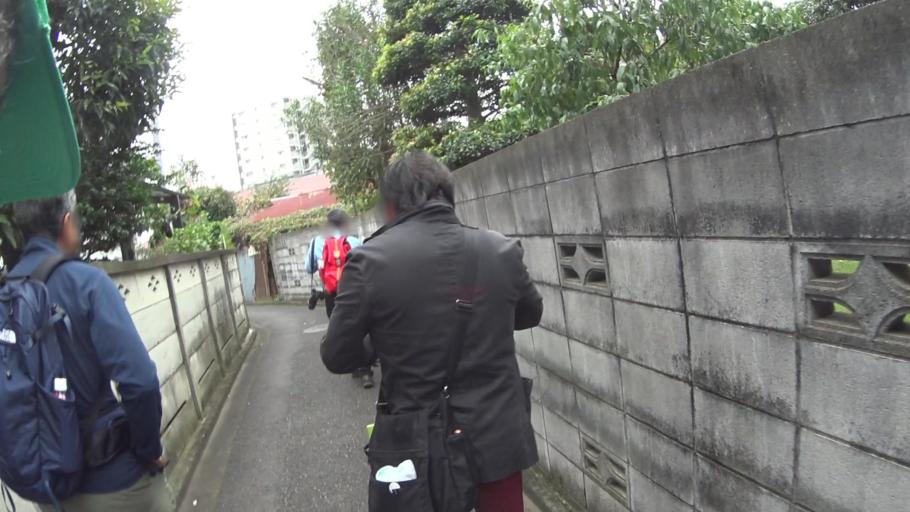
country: JP
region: Saitama
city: Hanno
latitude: 35.8546
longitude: 139.3202
